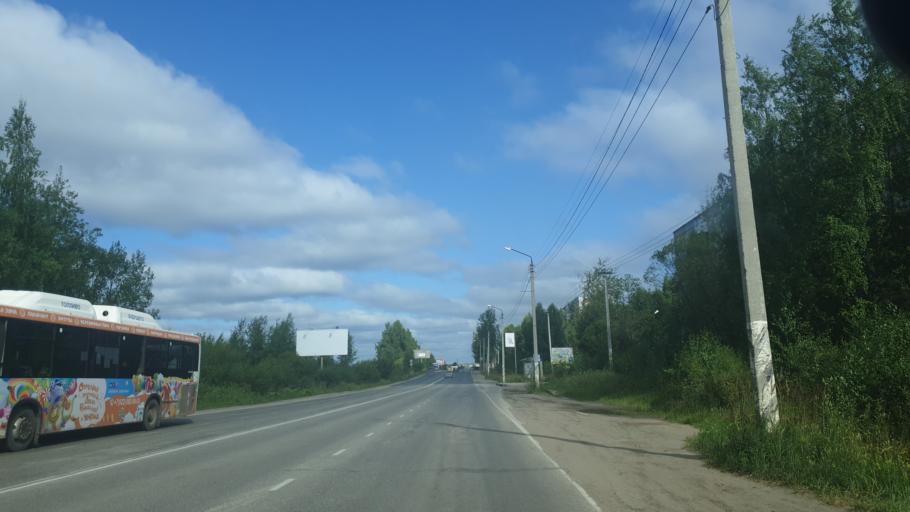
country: RU
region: Komi Republic
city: Ezhva
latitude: 61.7889
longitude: 50.7430
